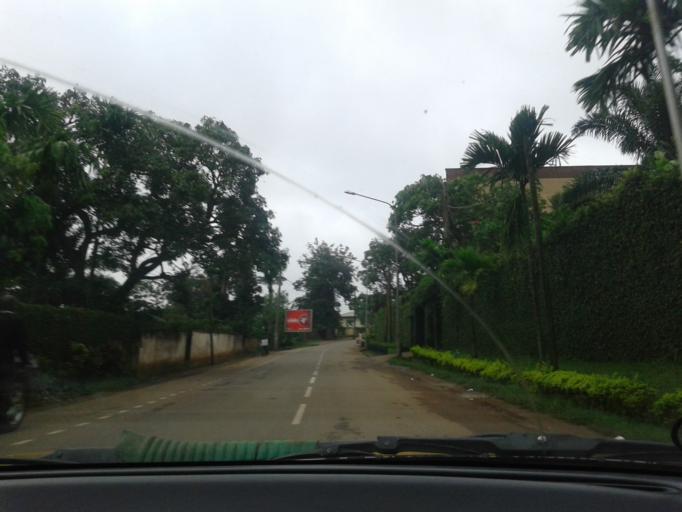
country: CM
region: Centre
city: Yaounde
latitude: 3.8741
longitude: 11.5187
